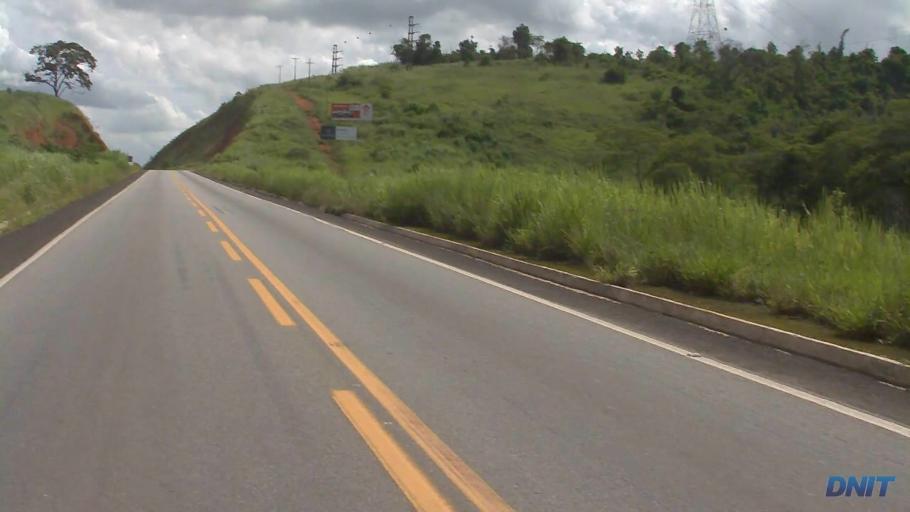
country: BR
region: Minas Gerais
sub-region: Ipatinga
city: Ipatinga
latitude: -19.4156
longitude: -42.4921
